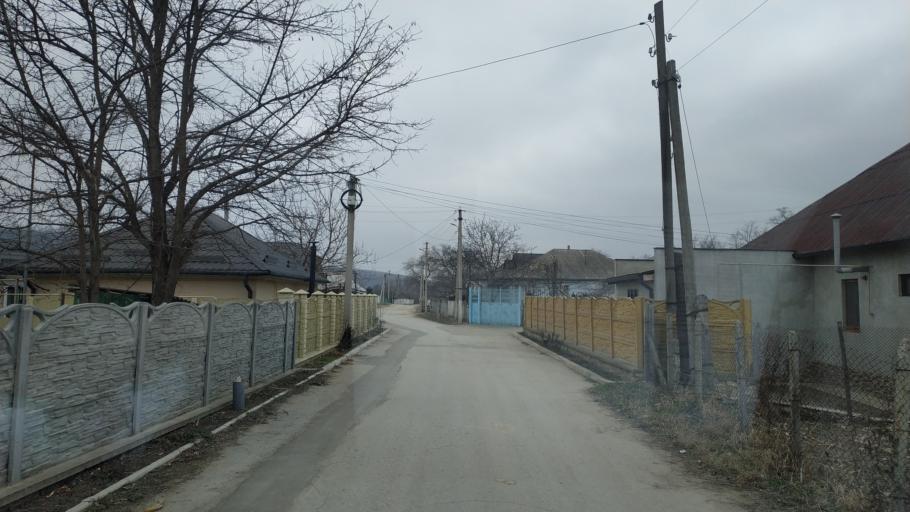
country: MD
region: Hincesti
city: Hincesti
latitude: 46.8852
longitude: 28.4060
